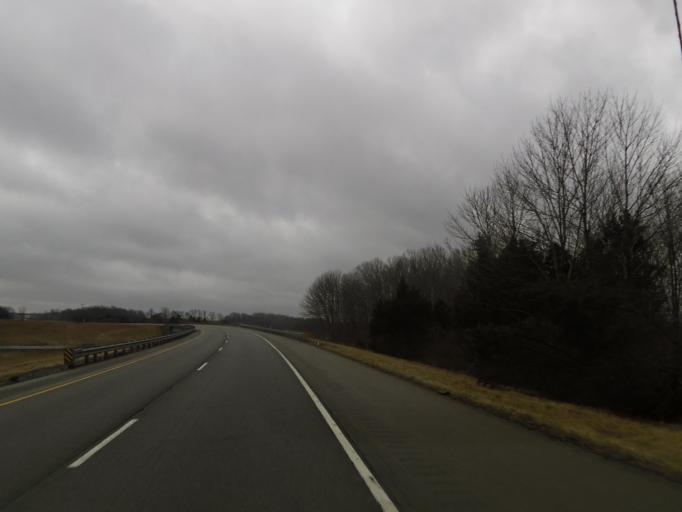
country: US
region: Illinois
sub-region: Johnson County
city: Goreville
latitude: 37.6047
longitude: -88.9980
